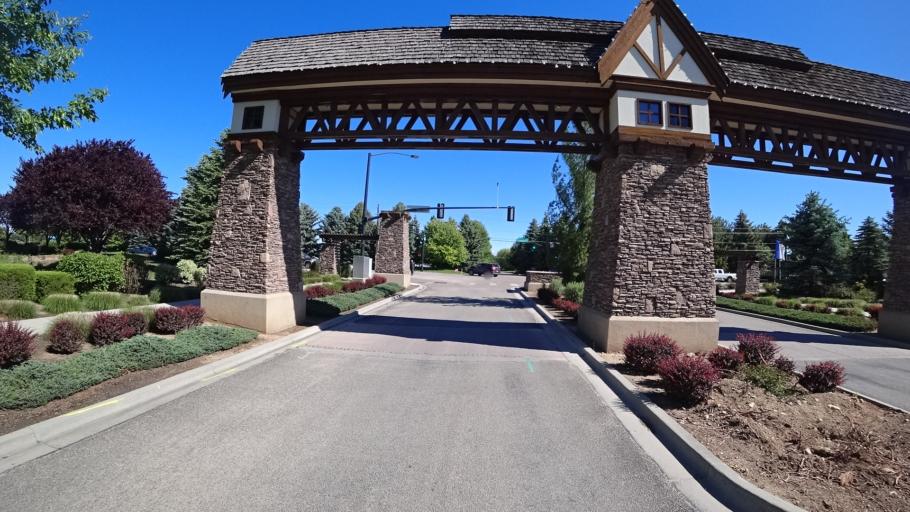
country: US
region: Idaho
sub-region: Ada County
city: Meridian
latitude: 43.6625
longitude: -116.4023
